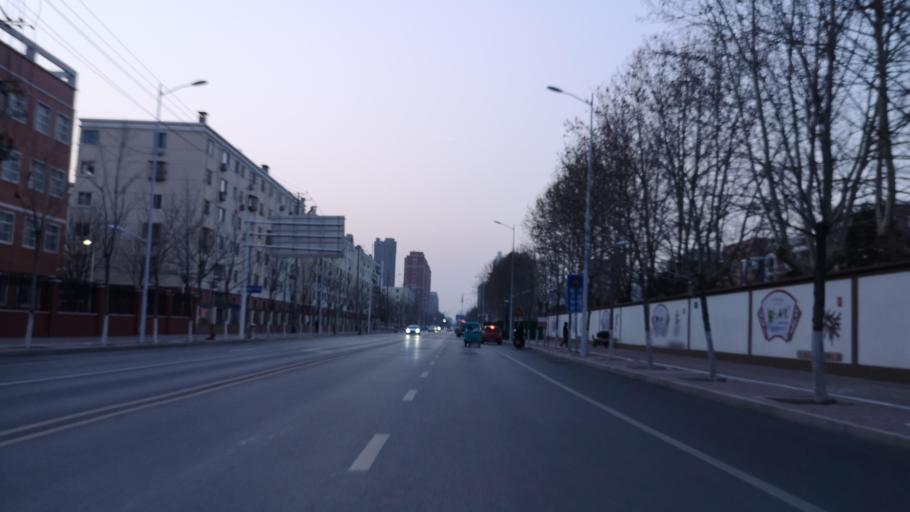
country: CN
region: Henan Sheng
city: Zhongyuanlu
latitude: 35.7633
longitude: 115.0620
